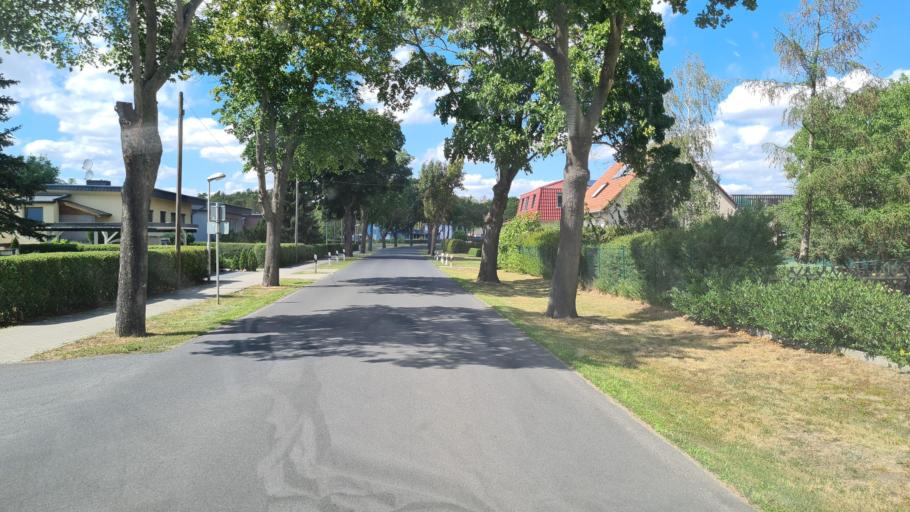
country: DE
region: Brandenburg
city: Trebbin
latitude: 52.1997
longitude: 13.2436
